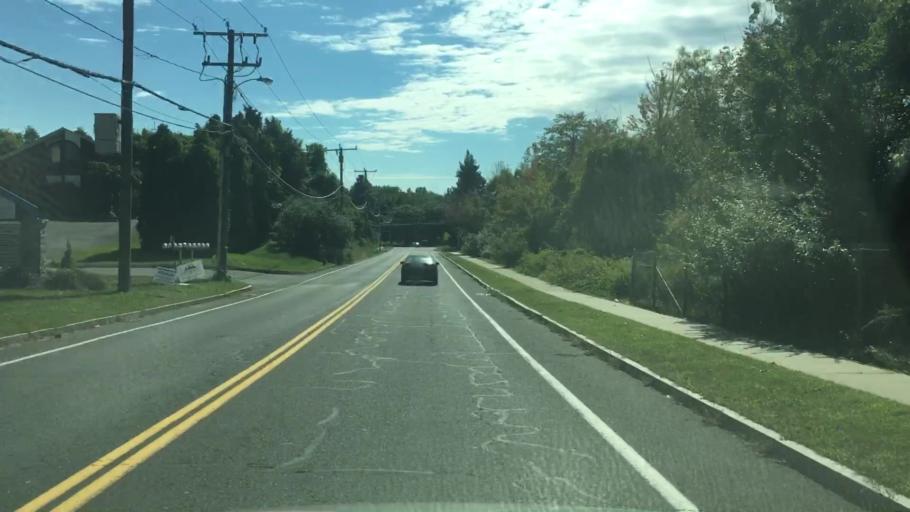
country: US
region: Connecticut
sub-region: Hartford County
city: Manchester
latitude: 41.8053
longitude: -72.5344
